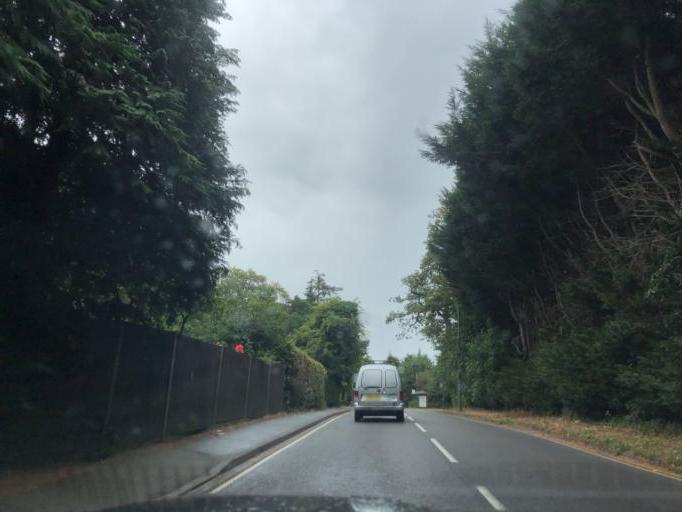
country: GB
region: England
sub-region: Surrey
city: Frimley
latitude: 51.3000
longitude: -0.7288
